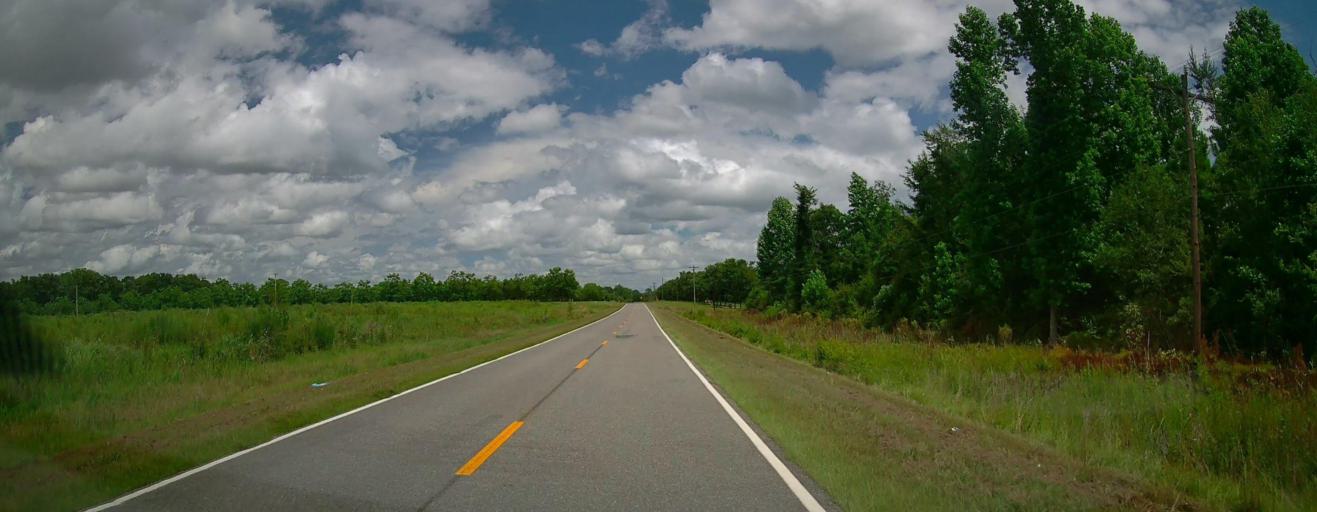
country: US
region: Georgia
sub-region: Irwin County
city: Ocilla
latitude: 31.6458
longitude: -83.2842
